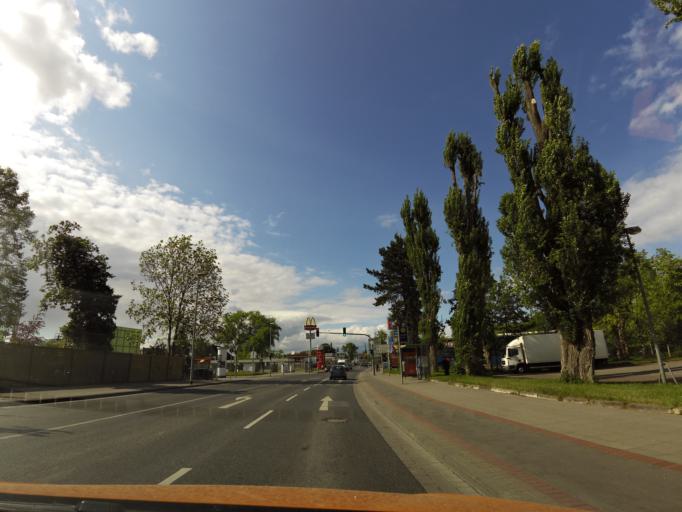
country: DE
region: Lower Saxony
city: Laatzen
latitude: 52.3802
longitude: 9.8626
